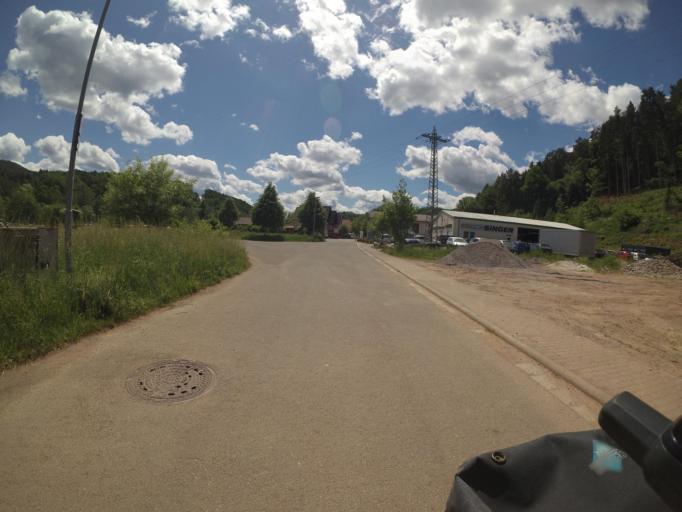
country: DE
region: Rheinland-Pfalz
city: Bruchweiler-Barenbach
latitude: 49.1219
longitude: 7.8012
